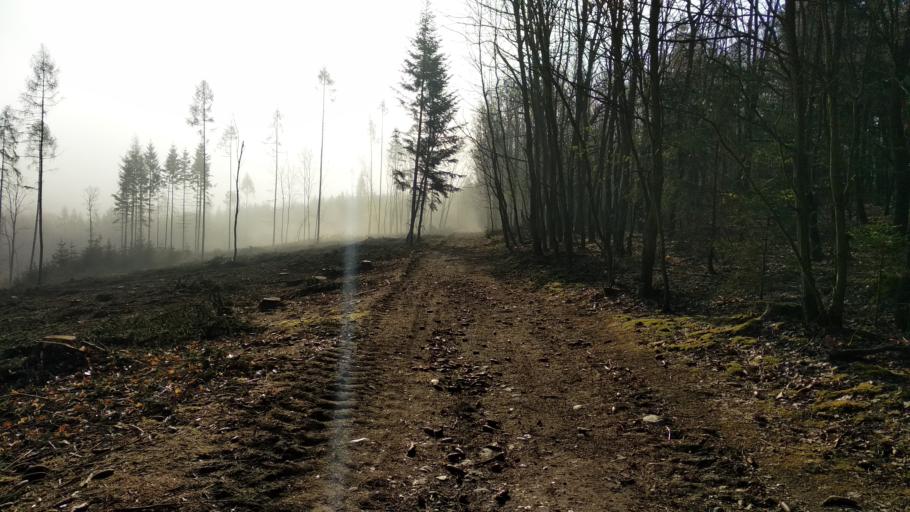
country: CZ
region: South Moravian
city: Drnovice
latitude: 49.2715
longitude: 16.9318
